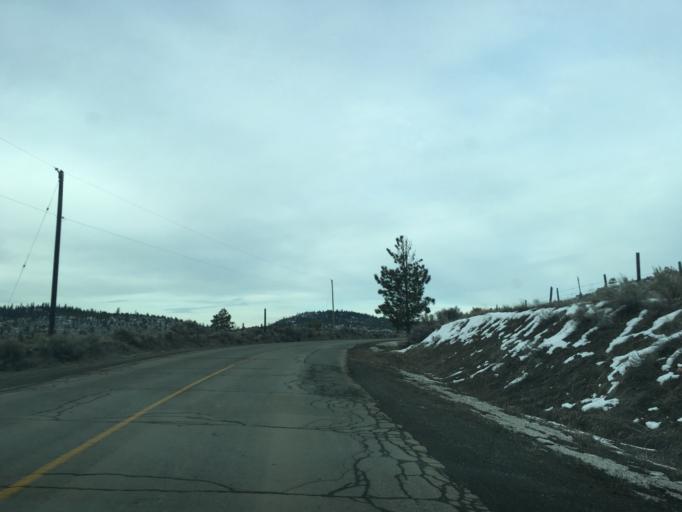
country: CA
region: British Columbia
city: Kamloops
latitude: 50.6232
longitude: -120.4435
